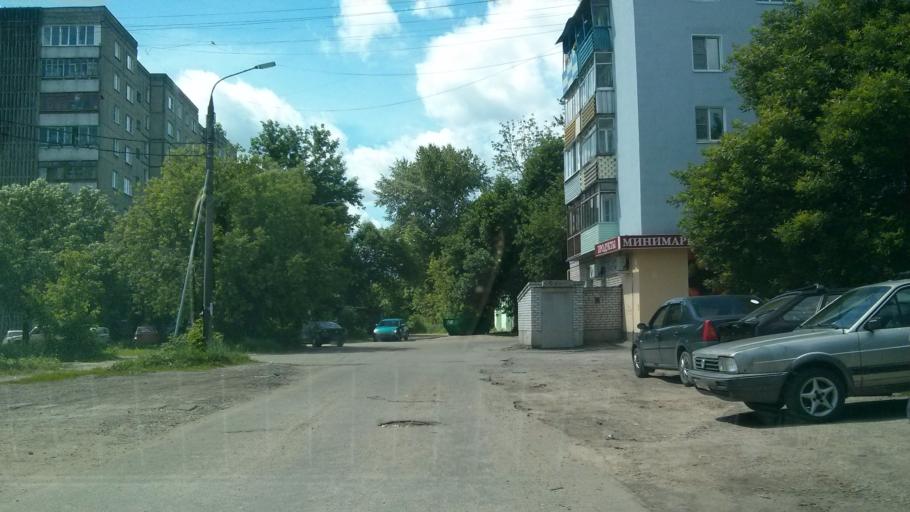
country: RU
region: Vladimir
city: Murom
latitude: 55.5676
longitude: 42.0654
